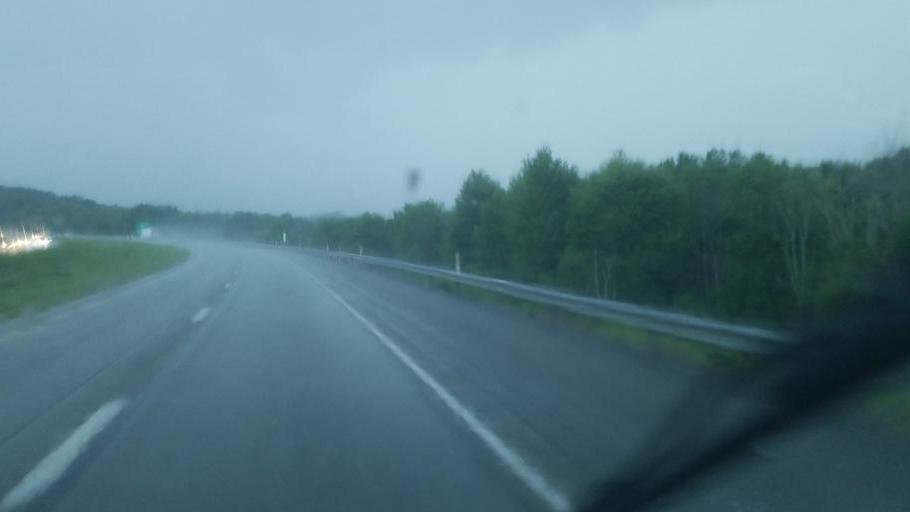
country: US
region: Pennsylvania
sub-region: Butler County
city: Prospect
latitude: 40.9533
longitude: -80.1420
